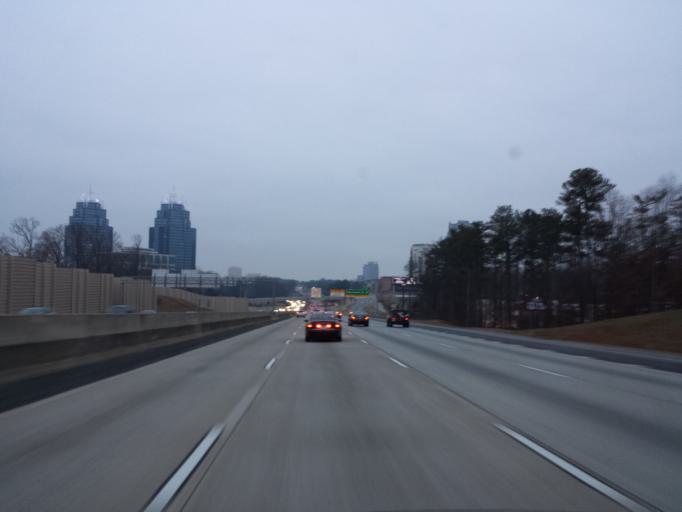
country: US
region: Georgia
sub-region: Fulton County
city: Sandy Springs
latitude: 33.9250
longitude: -84.3579
